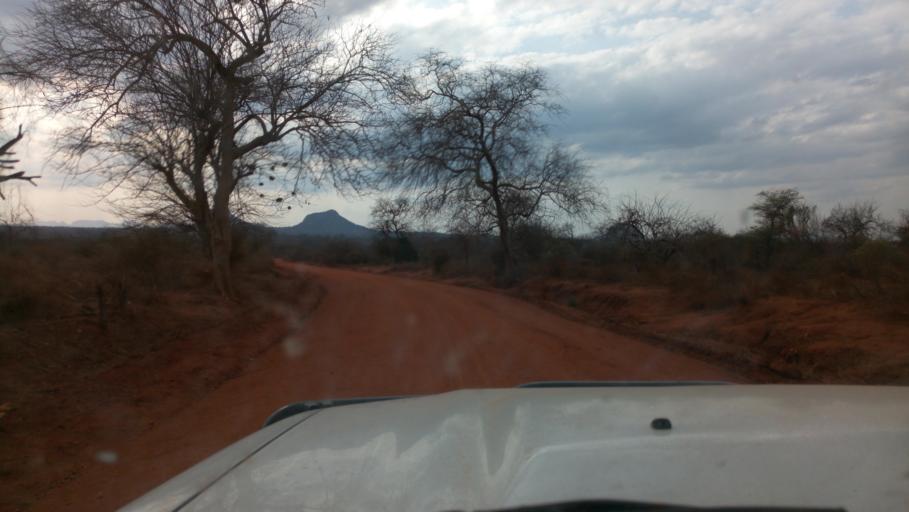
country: KE
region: Kitui
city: Kitui
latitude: -1.7329
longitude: 38.3982
